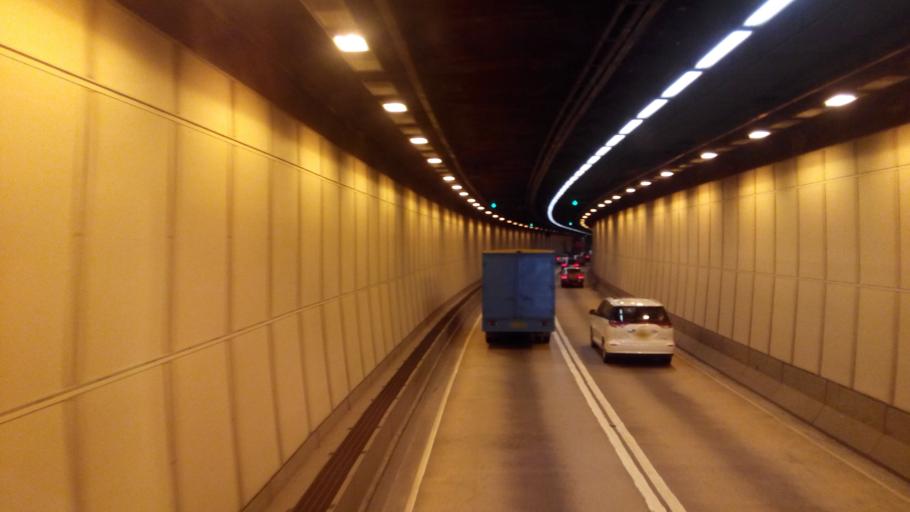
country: HK
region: Wanchai
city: Wan Chai
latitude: 22.2702
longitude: 114.1808
